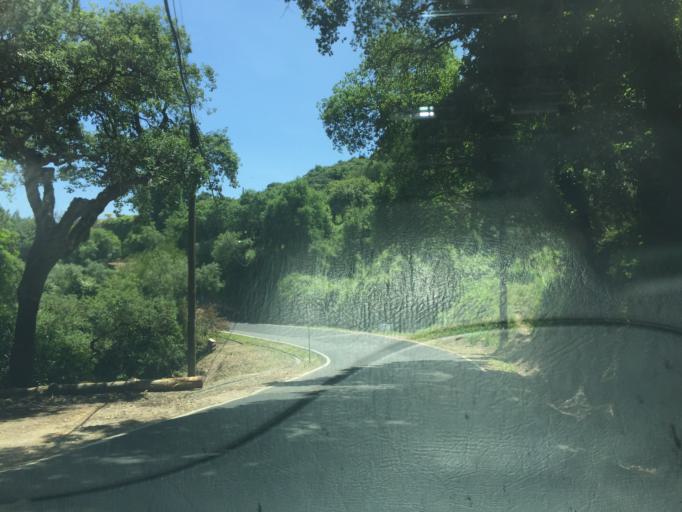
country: PT
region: Lisbon
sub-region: Mafra
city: Venda do Pinheiro
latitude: 38.8896
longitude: -9.2110
